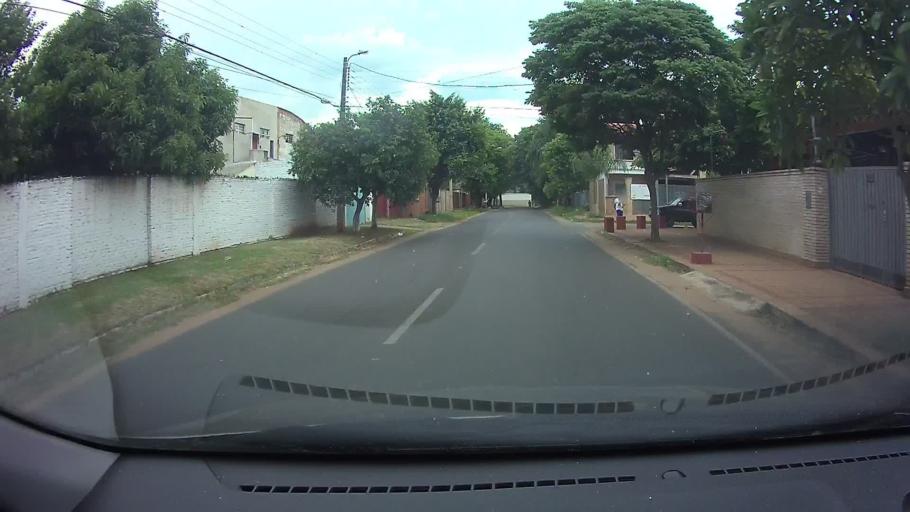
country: PY
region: Central
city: San Lorenzo
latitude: -25.2762
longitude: -57.4936
